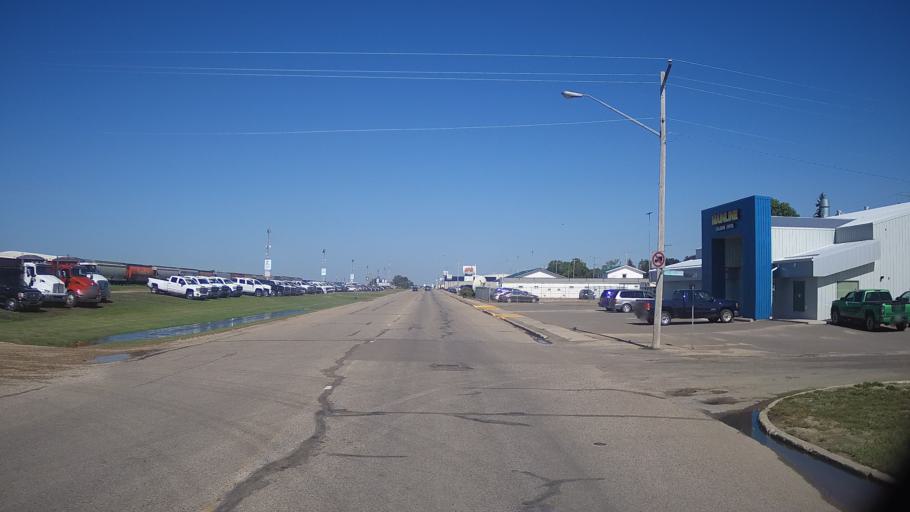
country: CA
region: Saskatchewan
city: Watrous
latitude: 51.6688
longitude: -105.4600
